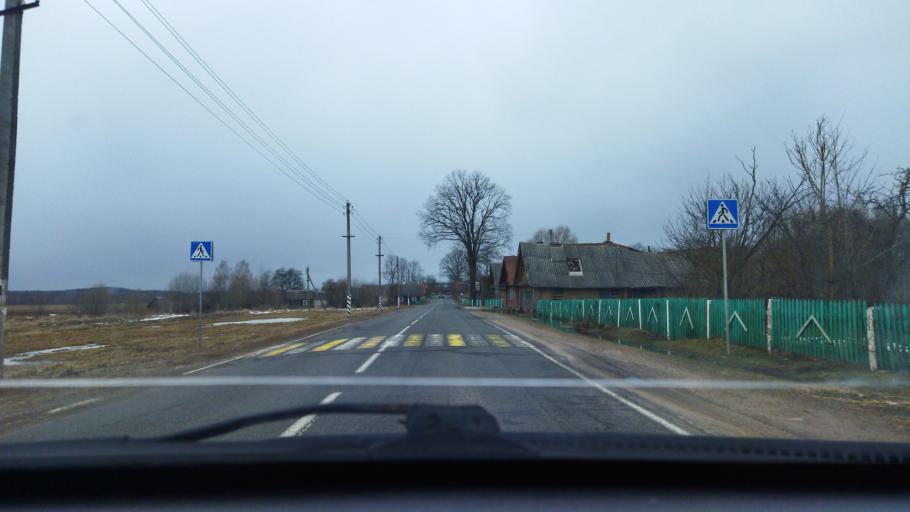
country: BY
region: Minsk
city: Svir
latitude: 54.8742
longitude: 26.3971
